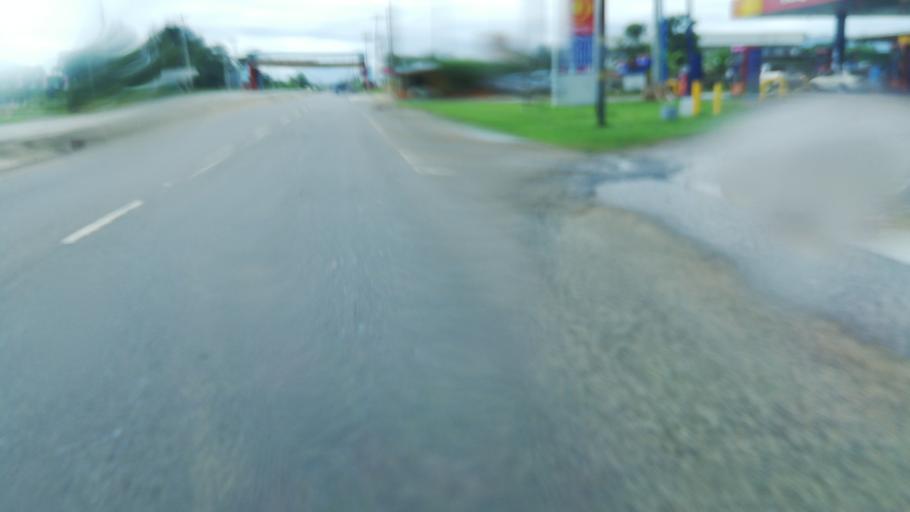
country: PA
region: Panama
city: Pacora
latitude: 9.0981
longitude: -79.2962
